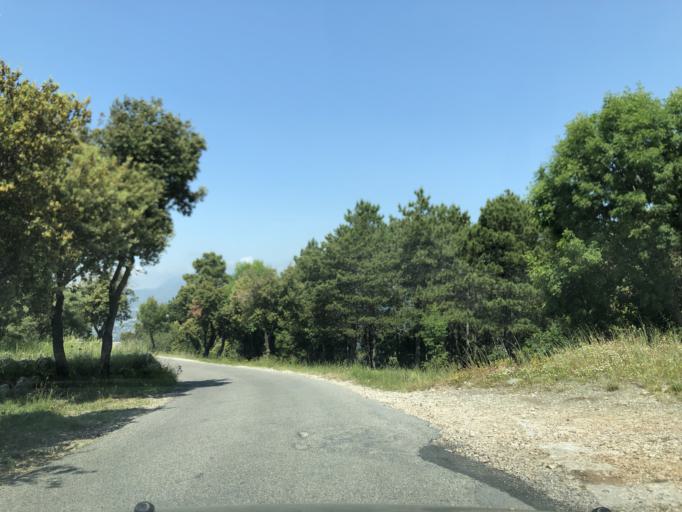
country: FR
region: Provence-Alpes-Cote d'Azur
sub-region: Departement des Alpes-Maritimes
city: Eze
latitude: 43.7396
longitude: 7.3472
